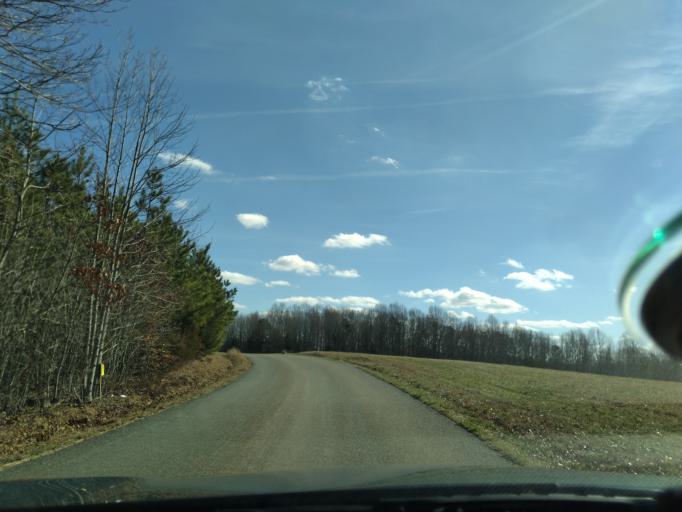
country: US
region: Virginia
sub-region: Nottoway County
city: Crewe
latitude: 37.1717
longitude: -78.2586
